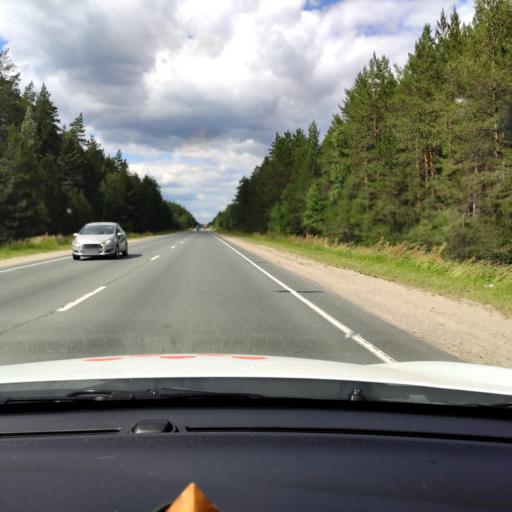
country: RU
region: Mariy-El
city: Krasnogorskiy
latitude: 56.0682
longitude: 48.3650
